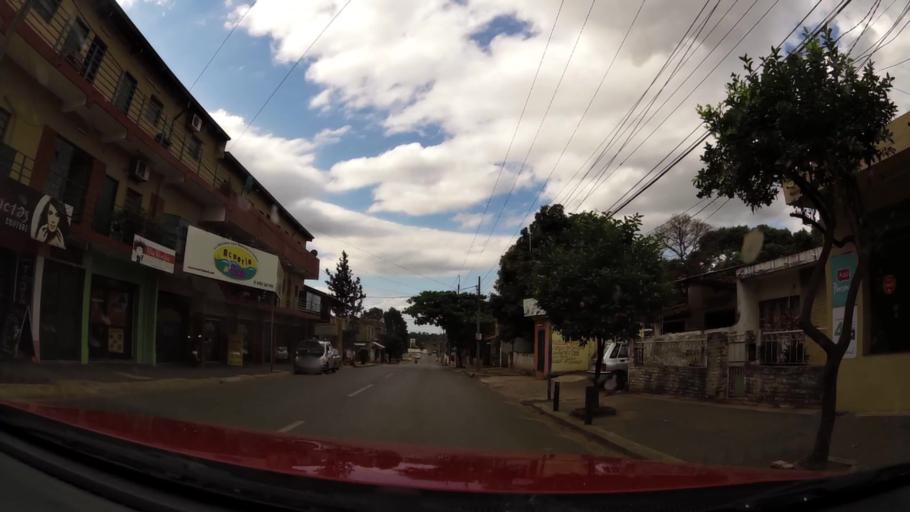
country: PY
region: Central
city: San Lorenzo
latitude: -25.2678
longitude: -57.5017
